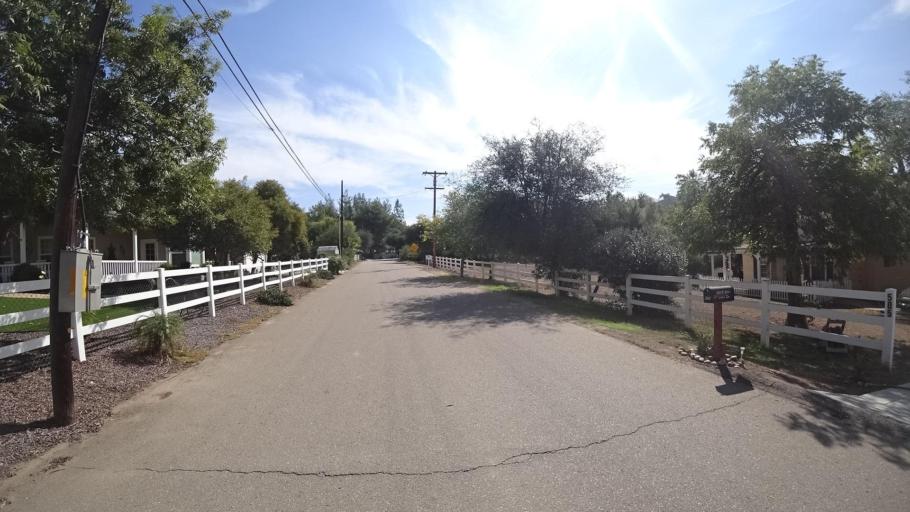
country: US
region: California
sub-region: San Diego County
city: Harbison Canyon
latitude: 32.8399
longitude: -116.8033
